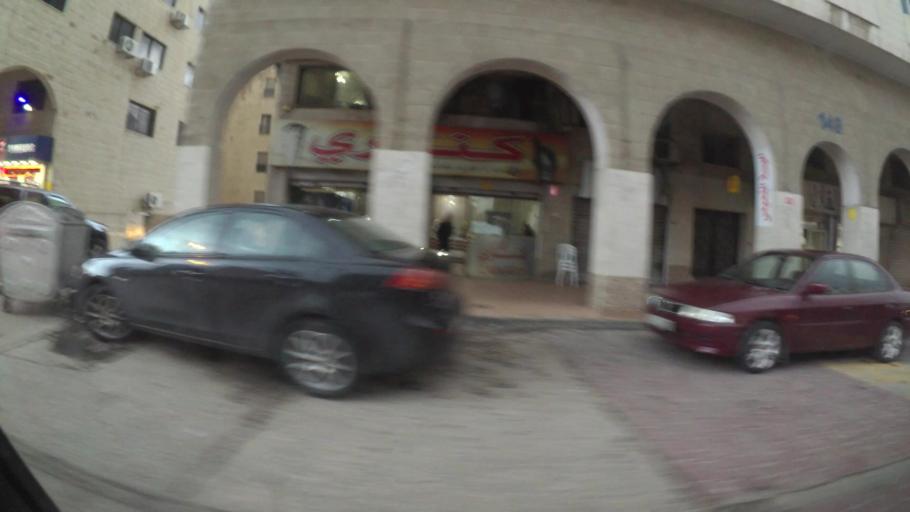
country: JO
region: Amman
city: Al Jubayhah
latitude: 31.9903
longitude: 35.8699
